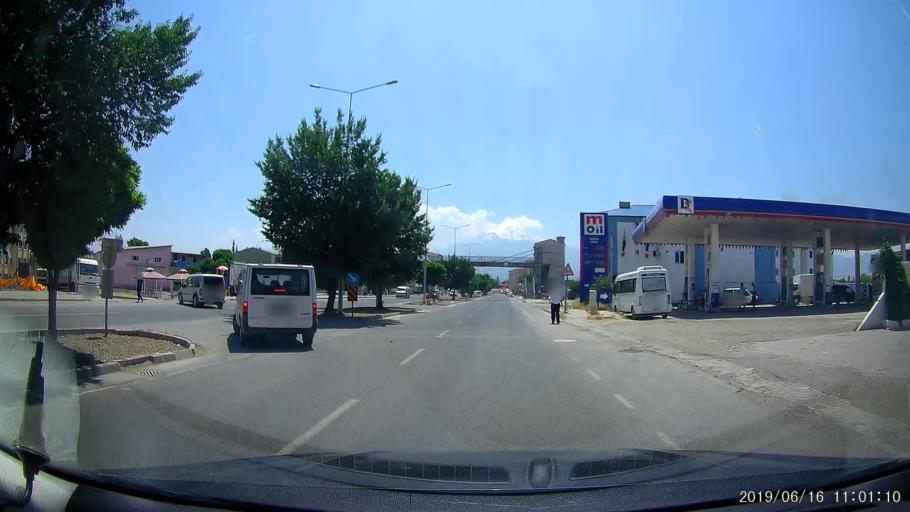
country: TR
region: Igdir
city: Igdir
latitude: 39.9168
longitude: 44.0476
